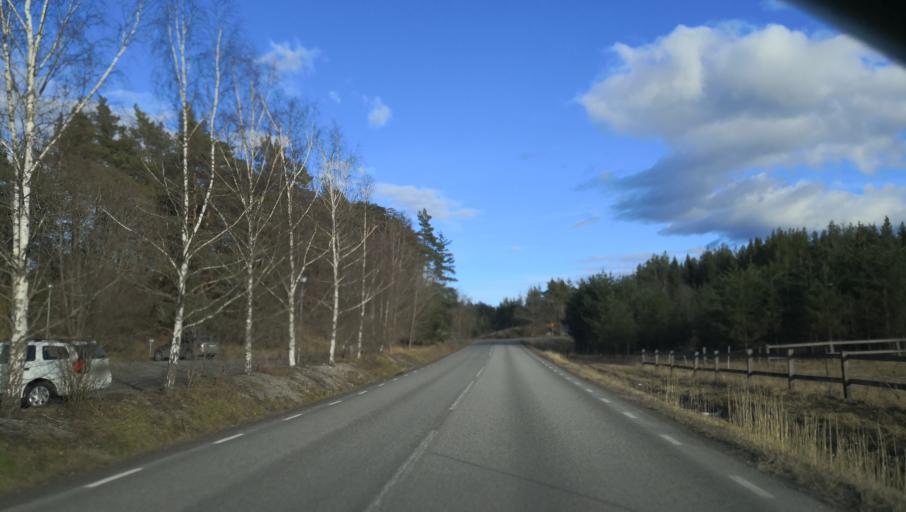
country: SE
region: Stockholm
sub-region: Varmdo Kommun
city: Gustavsberg
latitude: 59.3478
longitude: 18.3807
